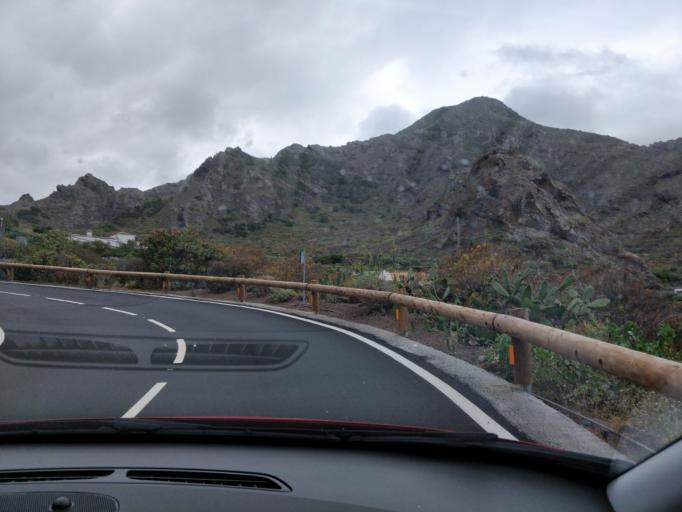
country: ES
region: Canary Islands
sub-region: Provincia de Santa Cruz de Tenerife
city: Tanque
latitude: 28.3527
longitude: -16.8449
